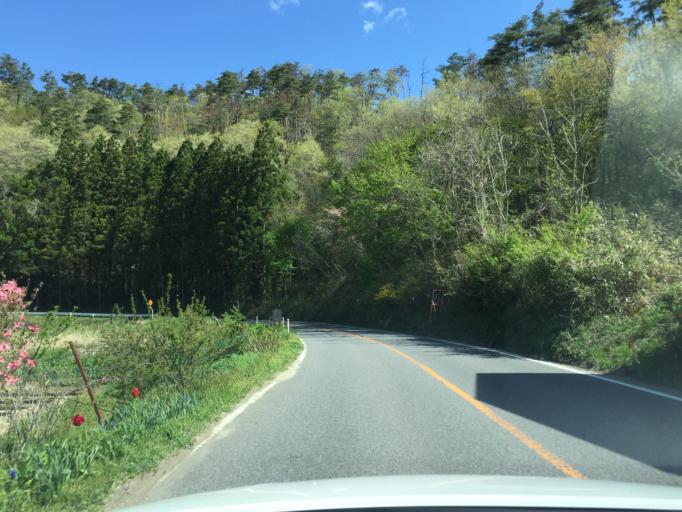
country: JP
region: Fukushima
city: Funehikimachi-funehiki
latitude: 37.5365
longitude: 140.5402
